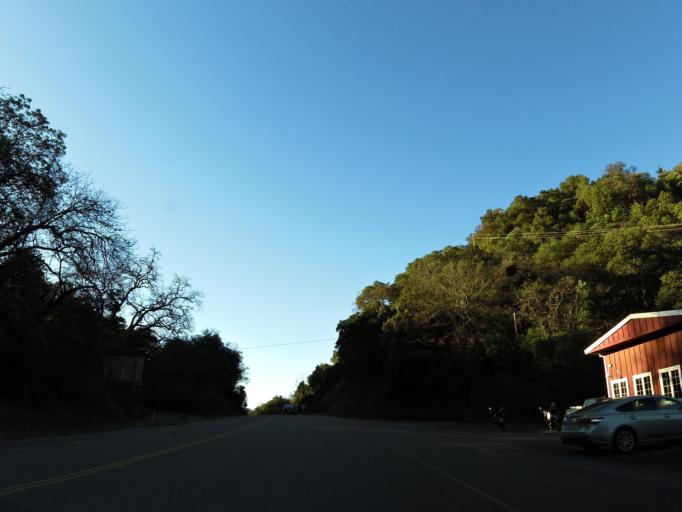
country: US
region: California
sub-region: Sonoma County
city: Cloverdale
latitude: 38.8182
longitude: -123.0229
